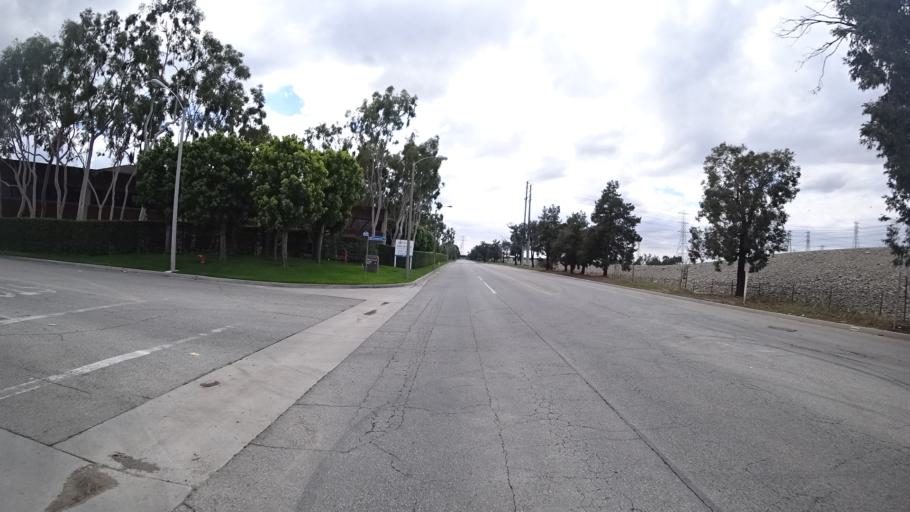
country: US
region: California
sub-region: Los Angeles County
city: Baldwin Park
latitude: 34.1025
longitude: -117.9796
